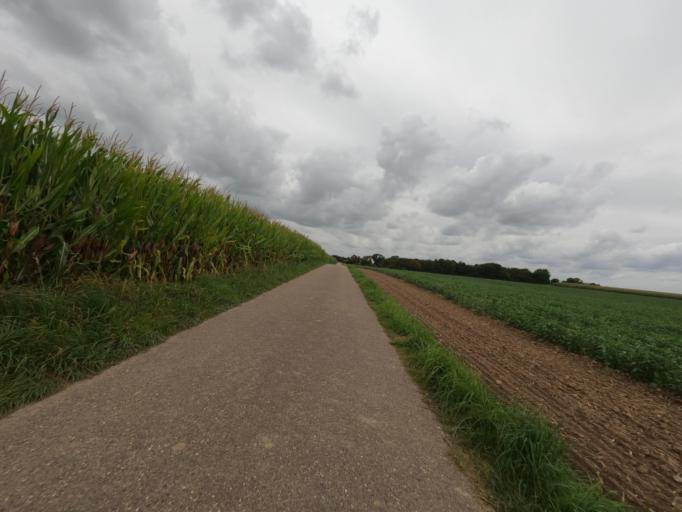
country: DE
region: North Rhine-Westphalia
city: Baesweiler
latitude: 50.9612
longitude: 6.1756
